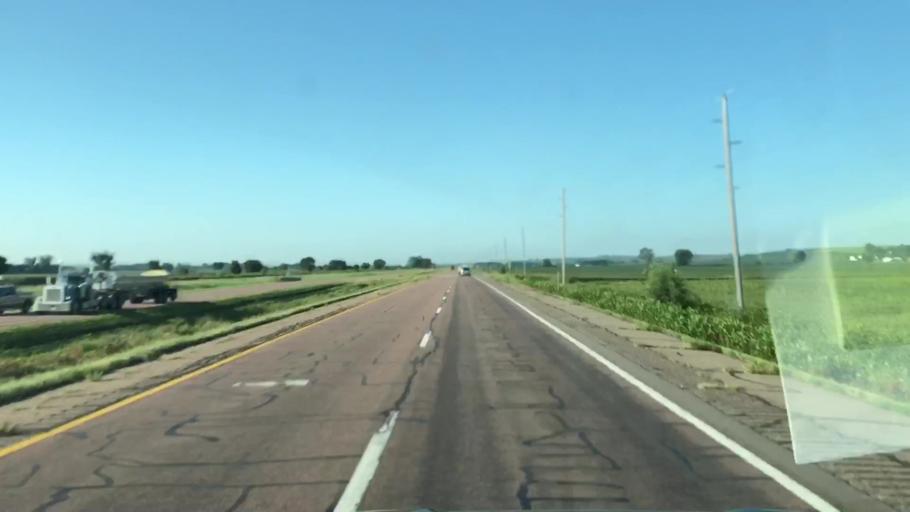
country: US
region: Iowa
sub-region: Plymouth County
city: Le Mars
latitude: 42.6938
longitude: -96.2616
